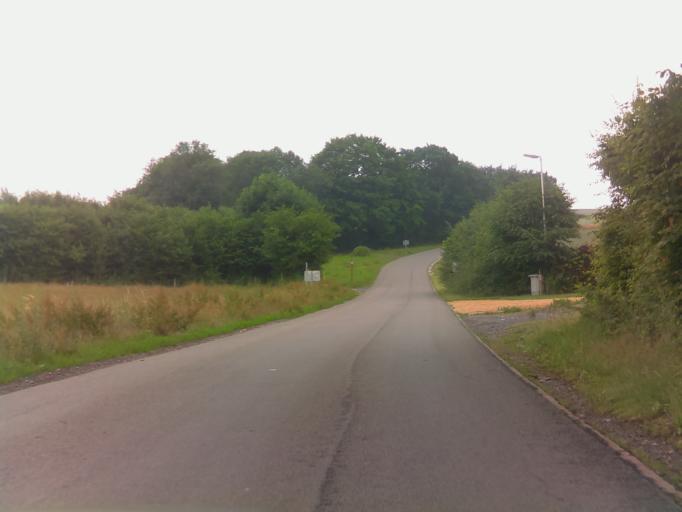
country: BE
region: Wallonia
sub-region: Province du Luxembourg
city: Leglise
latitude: 49.7975
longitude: 5.5406
